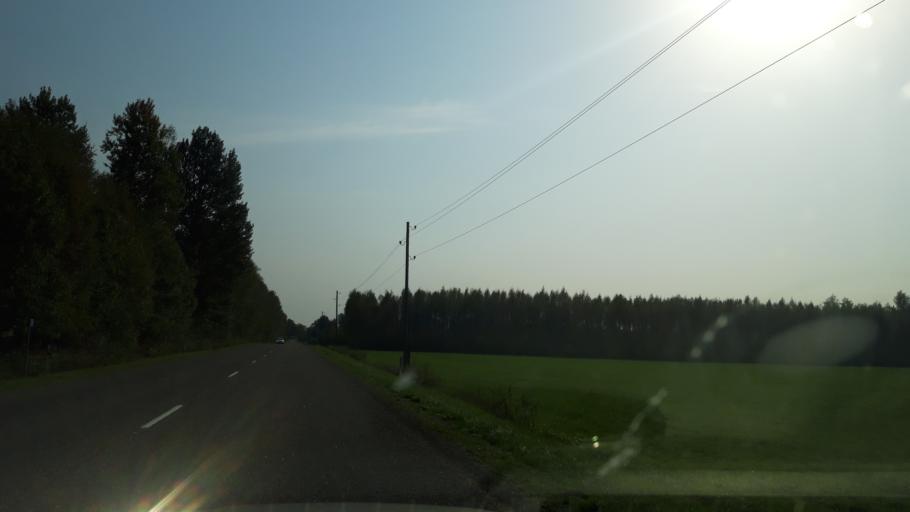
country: LV
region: Burtnieki
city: Matisi
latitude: 57.6327
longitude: 25.2599
